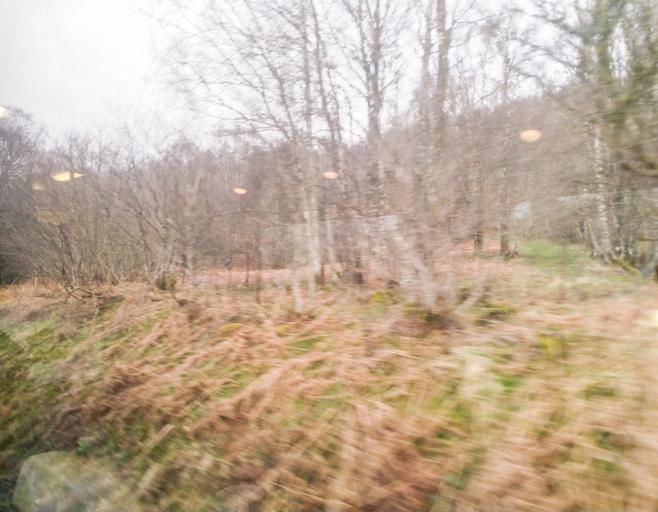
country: GB
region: Scotland
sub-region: Highland
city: Spean Bridge
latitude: 56.8854
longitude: -4.8166
